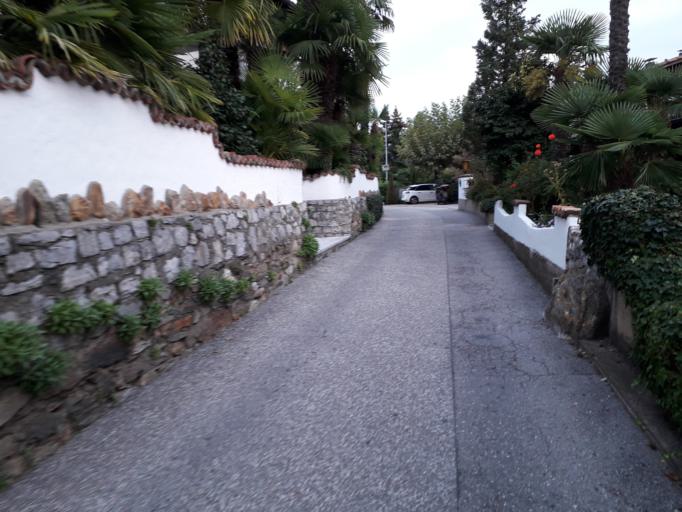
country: CH
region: Ticino
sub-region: Lugano District
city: Comano
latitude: 46.0354
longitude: 8.9566
